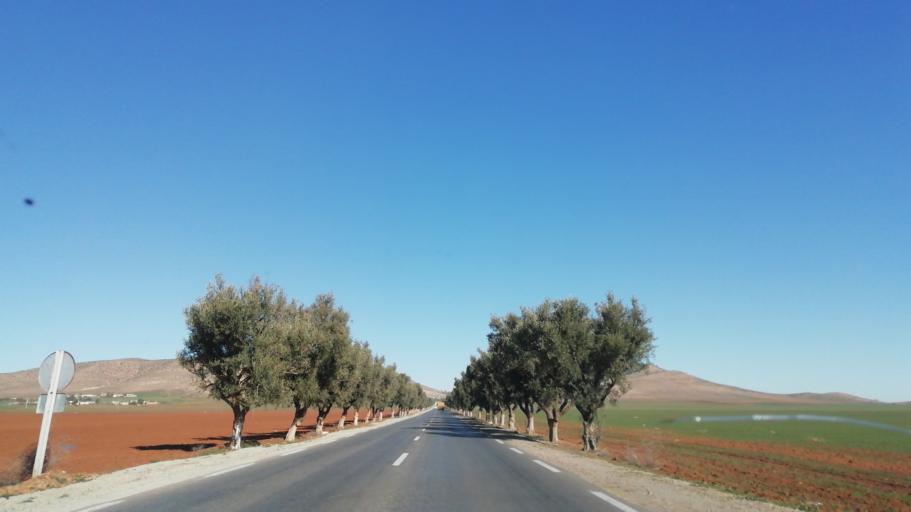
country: DZ
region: Mascara
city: Mascara
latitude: 35.2240
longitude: 0.1139
